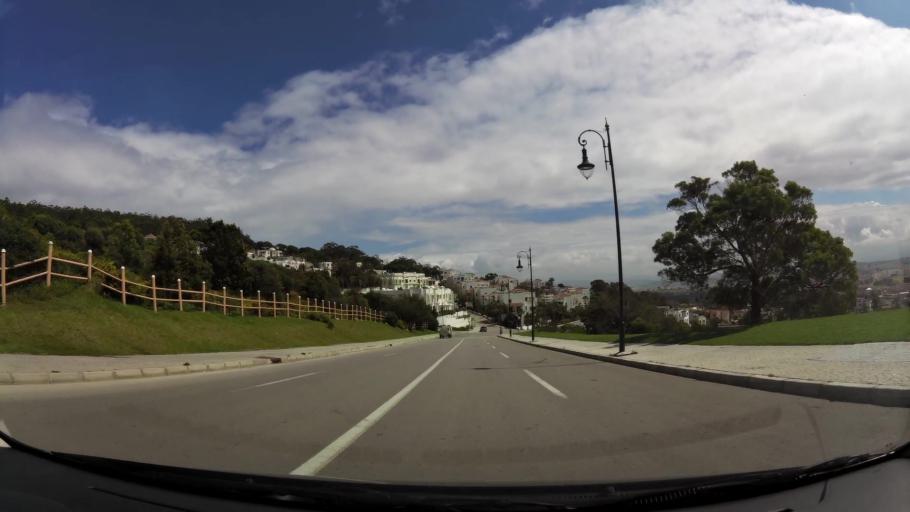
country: MA
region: Tanger-Tetouan
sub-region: Tanger-Assilah
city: Boukhalef
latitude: 35.7827
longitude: -5.8629
